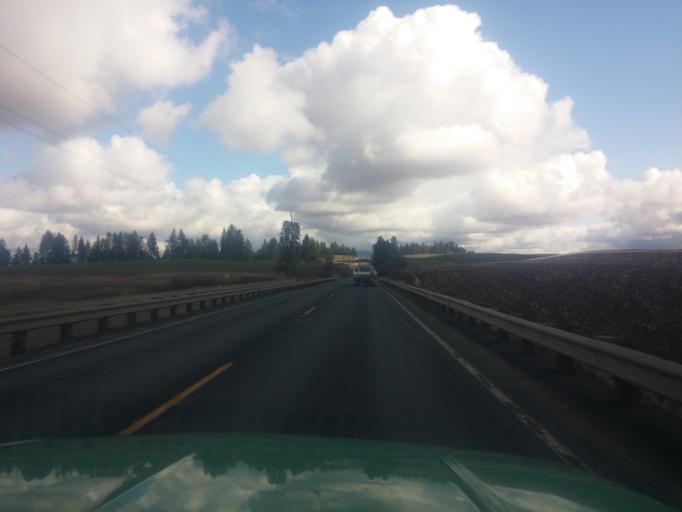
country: US
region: Idaho
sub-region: Latah County
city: Moscow
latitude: 46.9034
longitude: -116.9750
